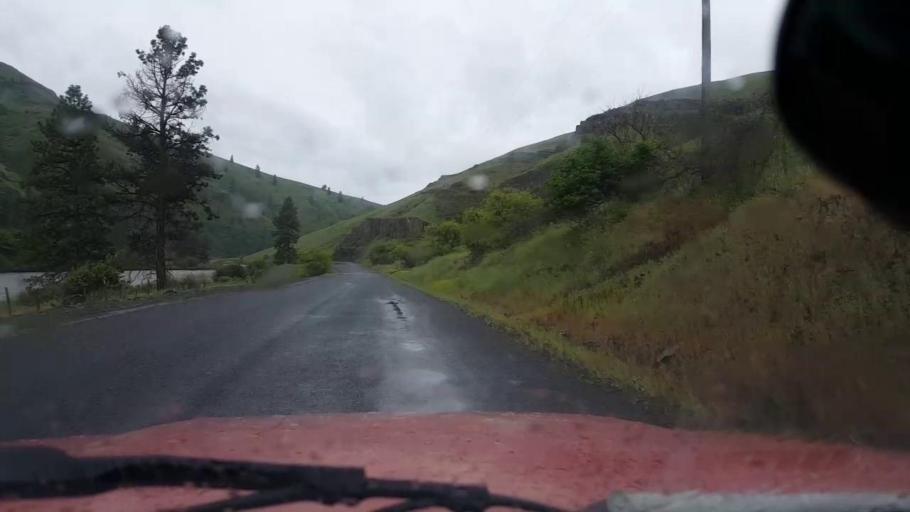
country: US
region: Washington
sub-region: Asotin County
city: Asotin
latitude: 46.0245
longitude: -117.3374
